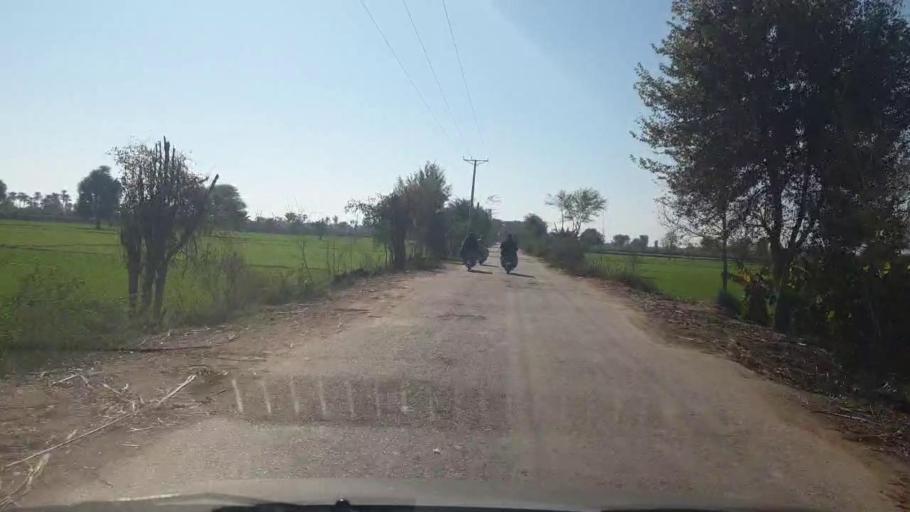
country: PK
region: Sindh
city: Bozdar
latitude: 27.2521
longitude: 68.6521
